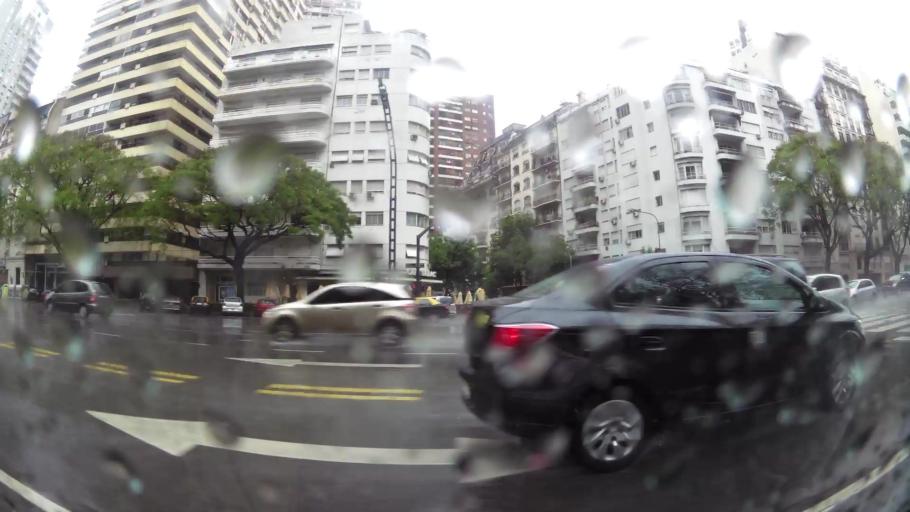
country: AR
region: Buenos Aires F.D.
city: Retiro
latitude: -34.5806
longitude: -58.4044
